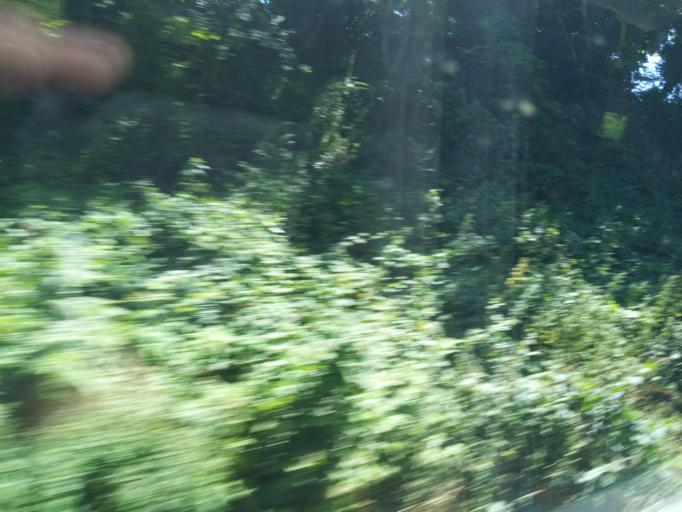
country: GB
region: England
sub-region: Cornwall
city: St Austell
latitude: 50.3416
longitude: -4.8168
